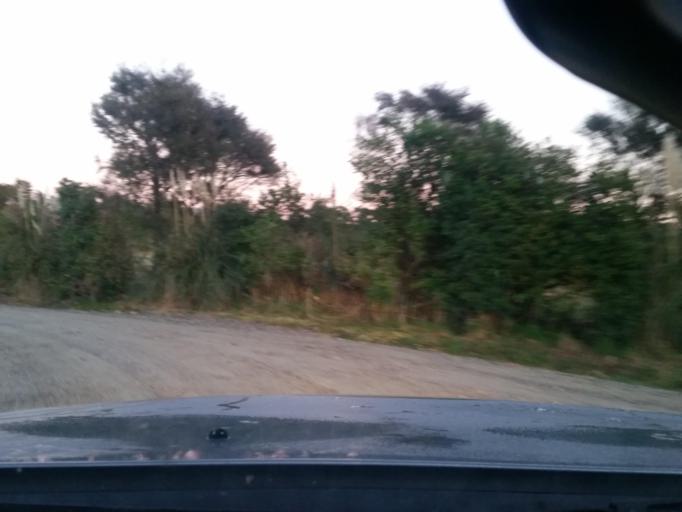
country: NZ
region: Tasman
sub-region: Tasman District
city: Takaka
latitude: -40.7016
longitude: 172.6701
